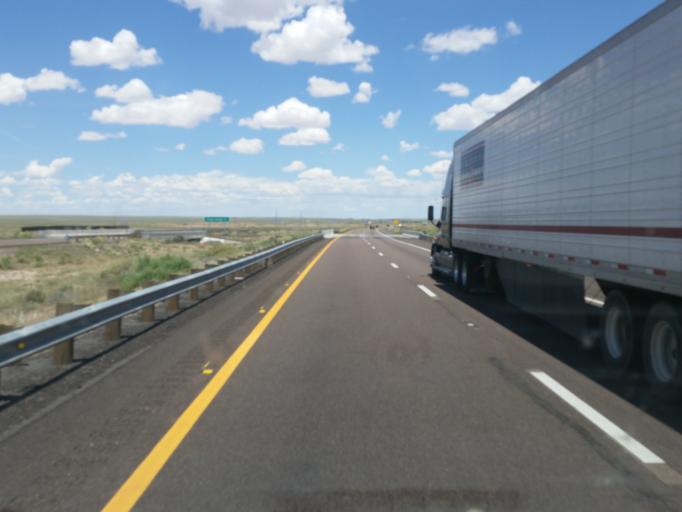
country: US
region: Arizona
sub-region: Navajo County
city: Holbrook
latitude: 34.9728
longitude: -110.0877
